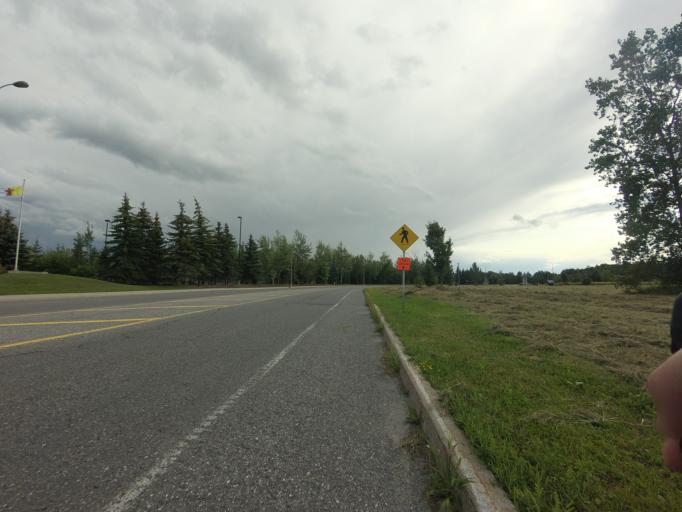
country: CA
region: Ontario
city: Ottawa
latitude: 45.2953
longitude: -75.7067
